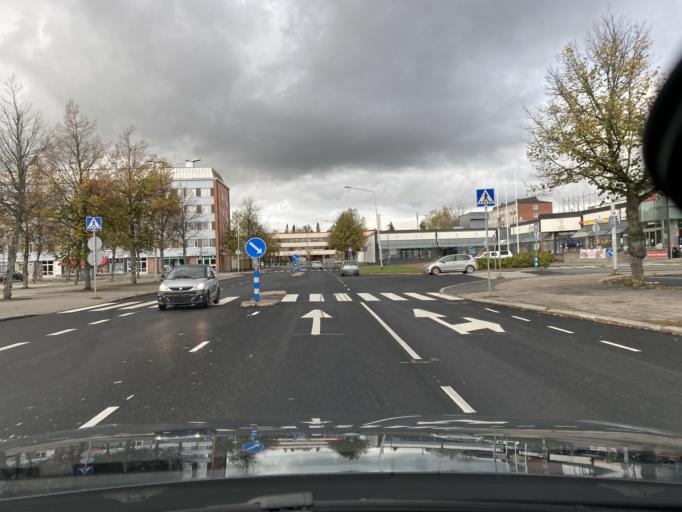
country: FI
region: Haeme
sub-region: Forssa
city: Forssa
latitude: 60.8158
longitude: 23.6297
